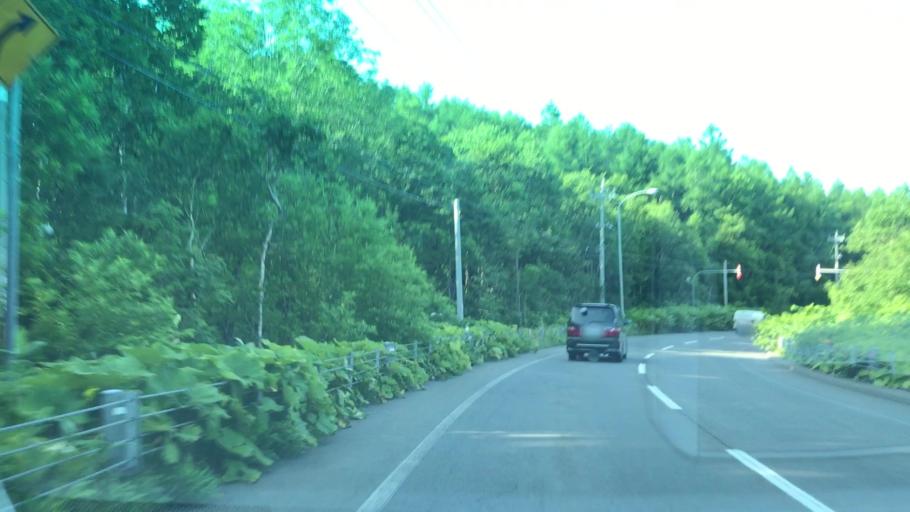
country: JP
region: Hokkaido
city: Otaru
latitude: 43.1089
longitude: 141.0051
